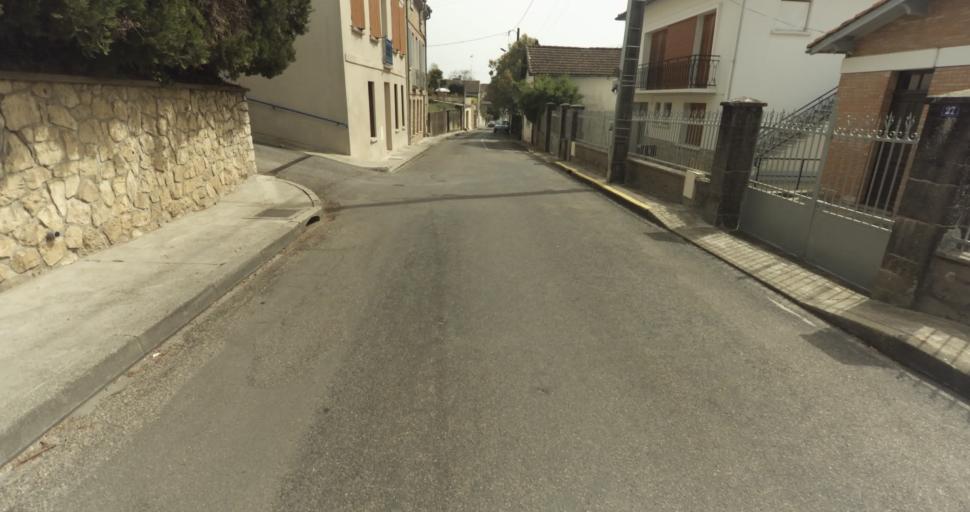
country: FR
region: Midi-Pyrenees
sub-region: Departement du Tarn-et-Garonne
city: Moissac
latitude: 44.1081
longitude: 1.0825
